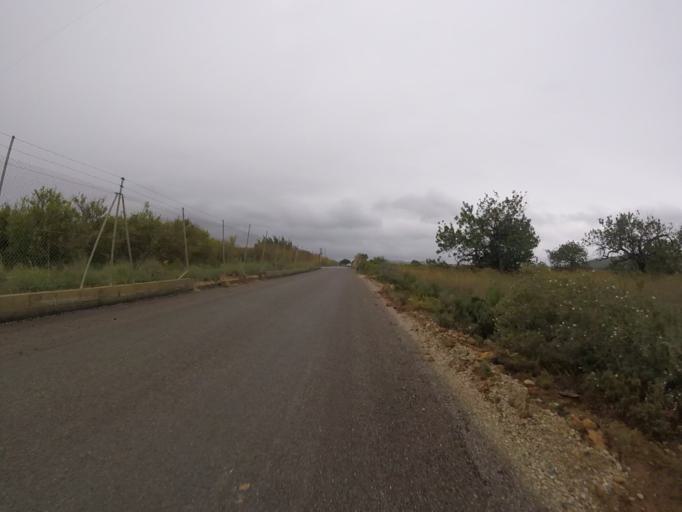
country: ES
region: Valencia
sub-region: Provincia de Castello
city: Alcoceber
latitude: 40.2381
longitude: 0.2510
